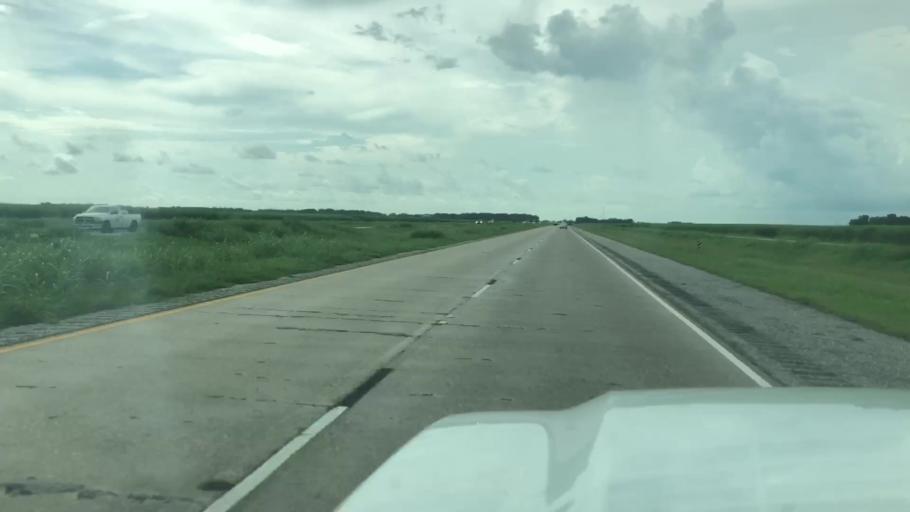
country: US
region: Louisiana
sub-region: Saint Mary Parish
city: Baldwin
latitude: 29.8475
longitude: -91.5902
